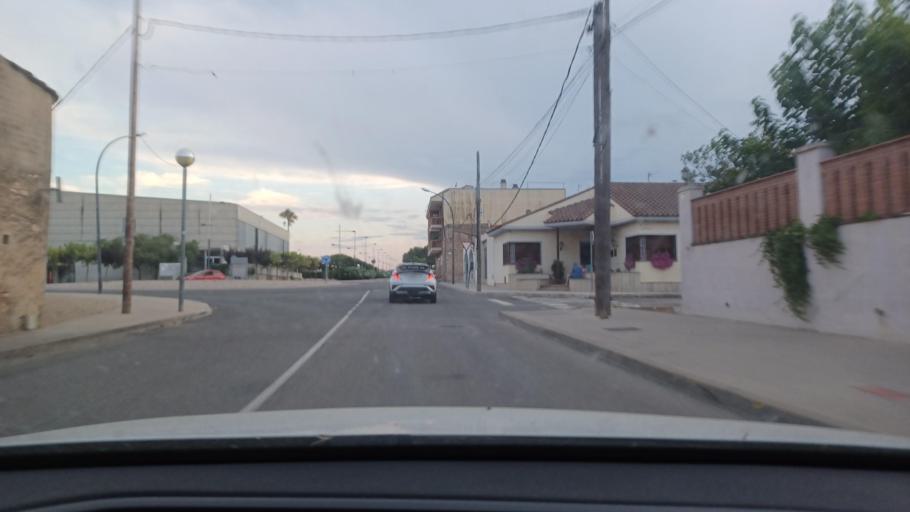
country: ES
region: Catalonia
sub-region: Provincia de Tarragona
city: Santa Barbara
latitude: 40.7135
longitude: 0.4893
